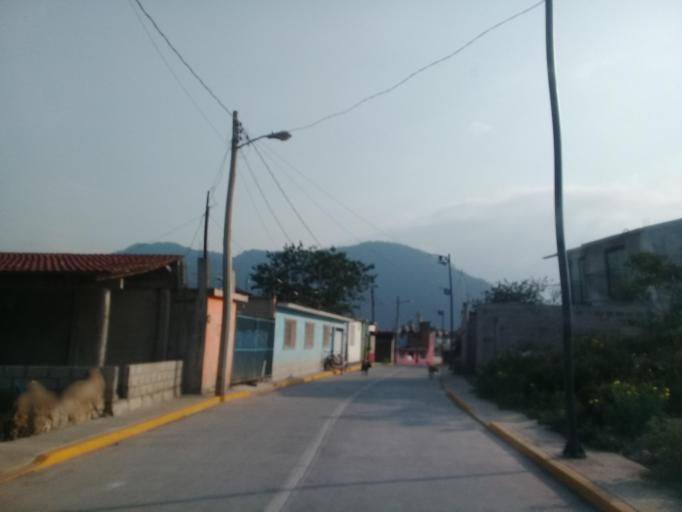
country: MX
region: Veracruz
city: Ixtac Zoquitlan
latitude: 18.8557
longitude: -97.0538
